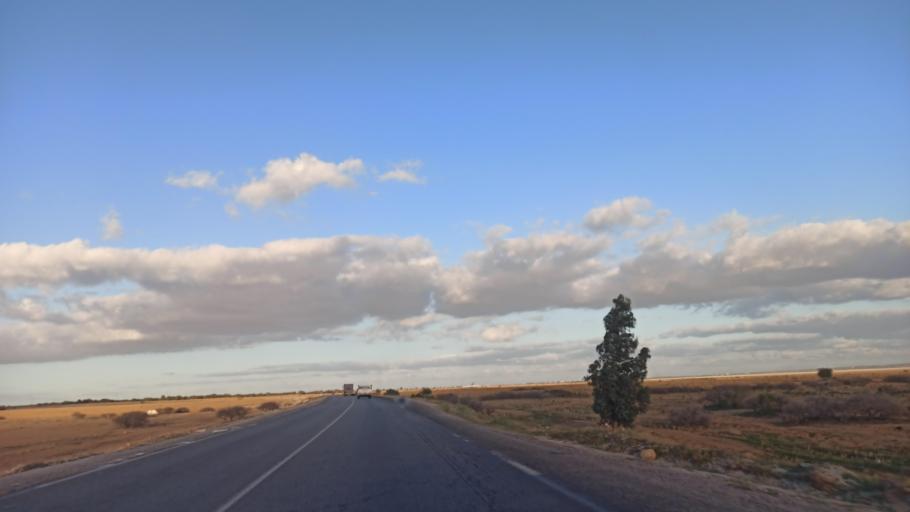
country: TN
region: Susah
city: Sidi Bou Ali
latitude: 35.8950
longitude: 10.2530
